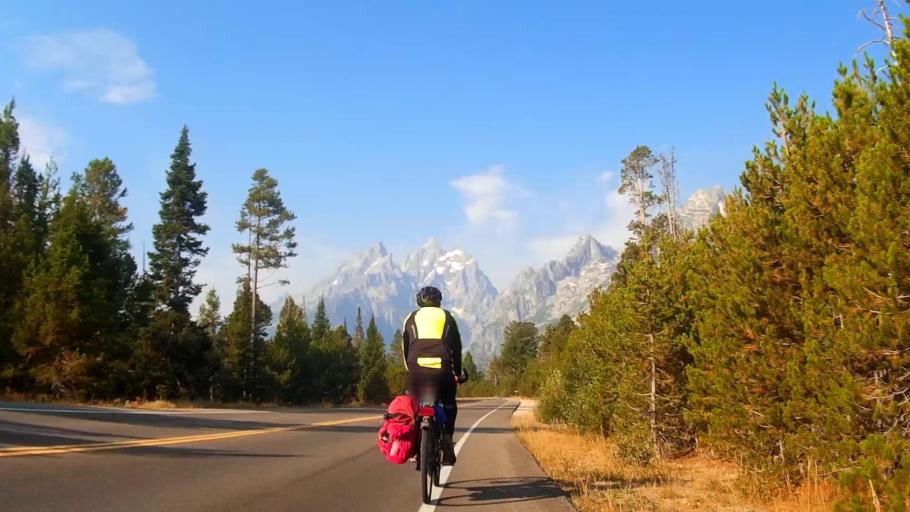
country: US
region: Wyoming
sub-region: Teton County
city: Moose Wilson Road
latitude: 43.7922
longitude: -110.7084
